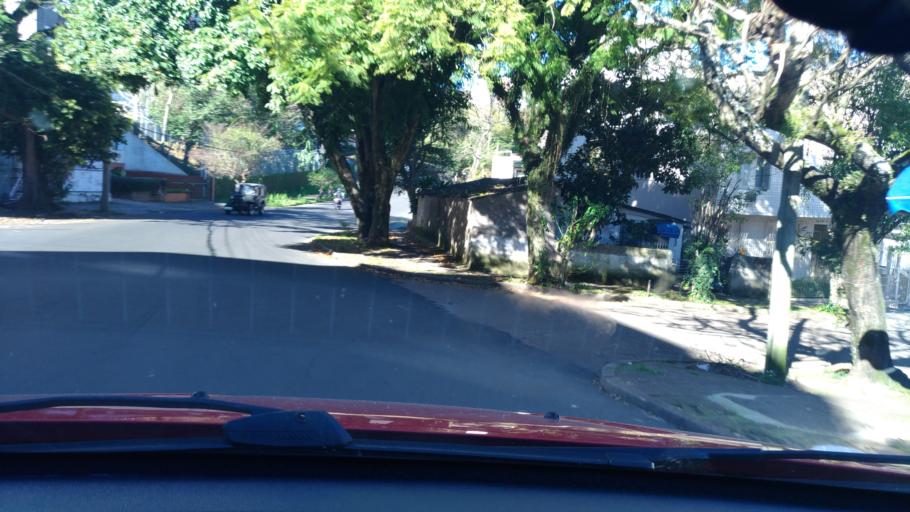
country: BR
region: Rio Grande do Sul
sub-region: Porto Alegre
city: Porto Alegre
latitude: -30.0092
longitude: -51.1641
